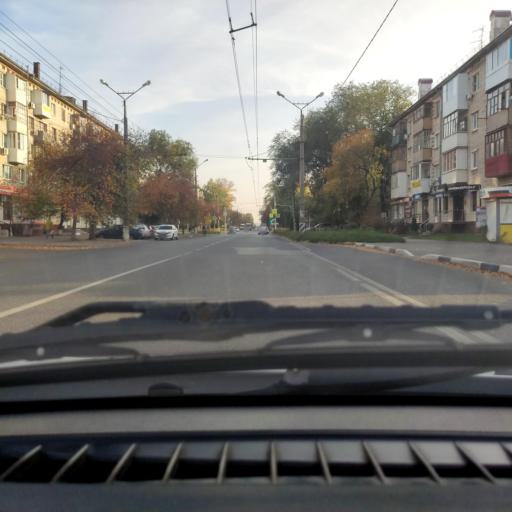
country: RU
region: Samara
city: Tol'yatti
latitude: 53.5175
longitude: 49.4163
